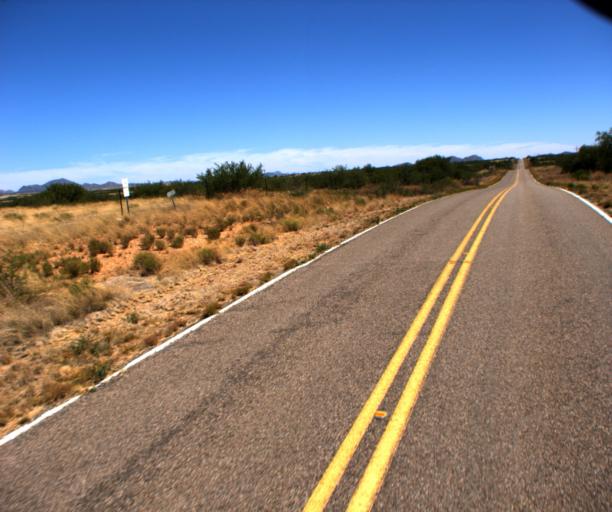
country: US
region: Arizona
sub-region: Pima County
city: Sells
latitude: 31.5647
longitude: -111.5386
